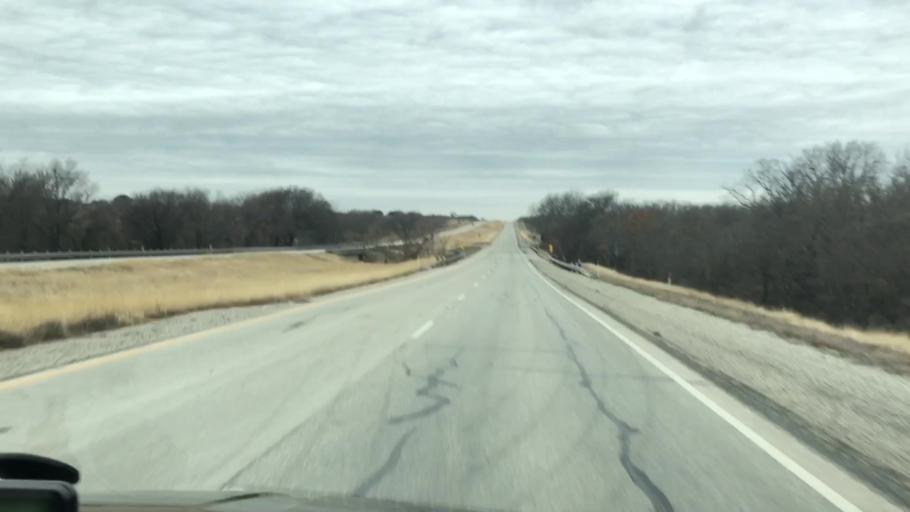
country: US
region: Texas
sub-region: Jack County
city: Jacksboro
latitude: 33.2400
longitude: -98.2166
